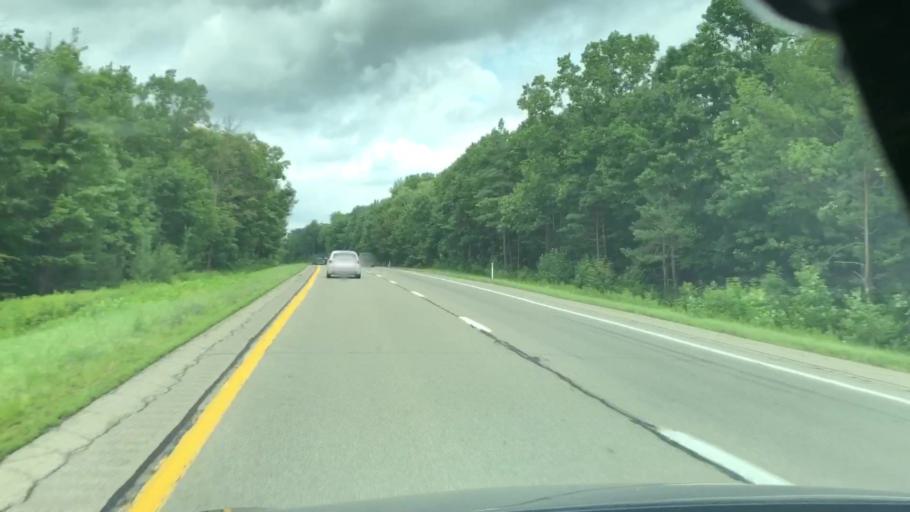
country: US
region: Pennsylvania
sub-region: Erie County
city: Edinboro
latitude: 41.7952
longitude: -80.1752
